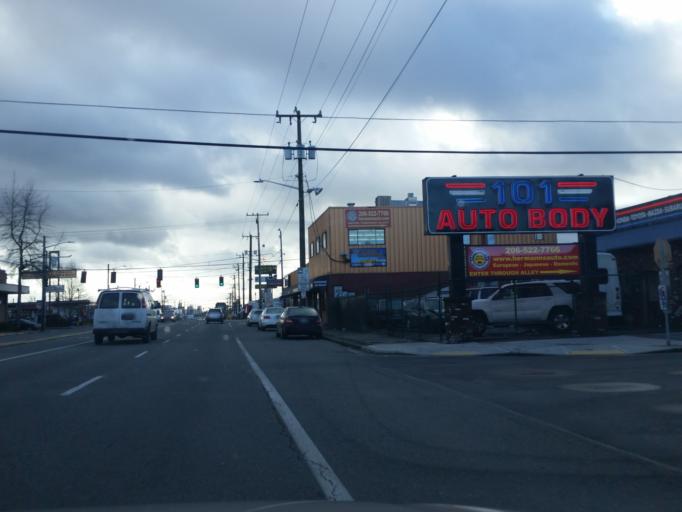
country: US
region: Washington
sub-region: King County
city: Shoreline
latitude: 47.7023
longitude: -122.3448
